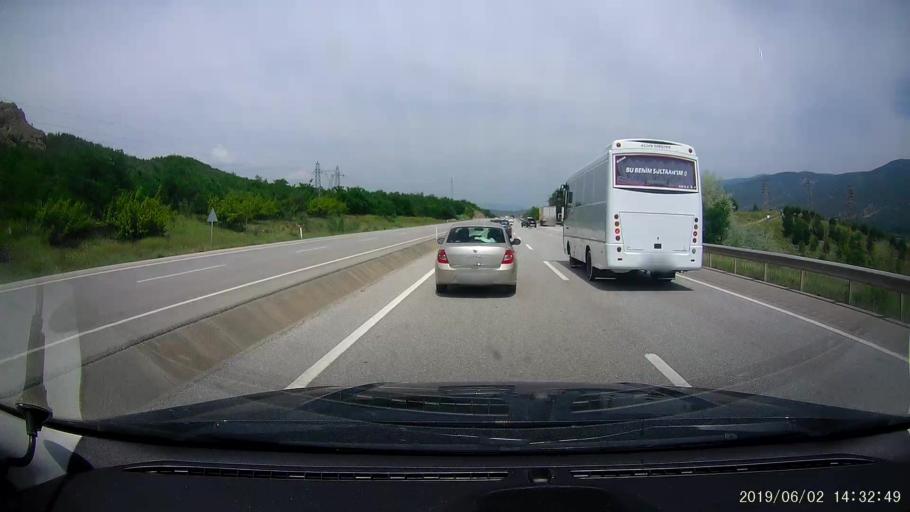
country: TR
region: Kastamonu
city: Tosya
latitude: 41.0273
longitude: 34.1565
